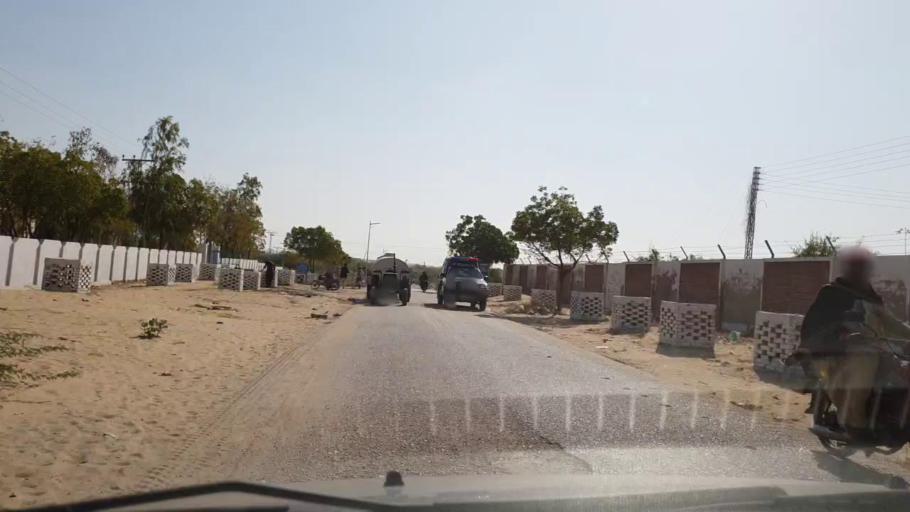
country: PK
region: Sindh
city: Diplo
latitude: 24.4772
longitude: 69.5806
